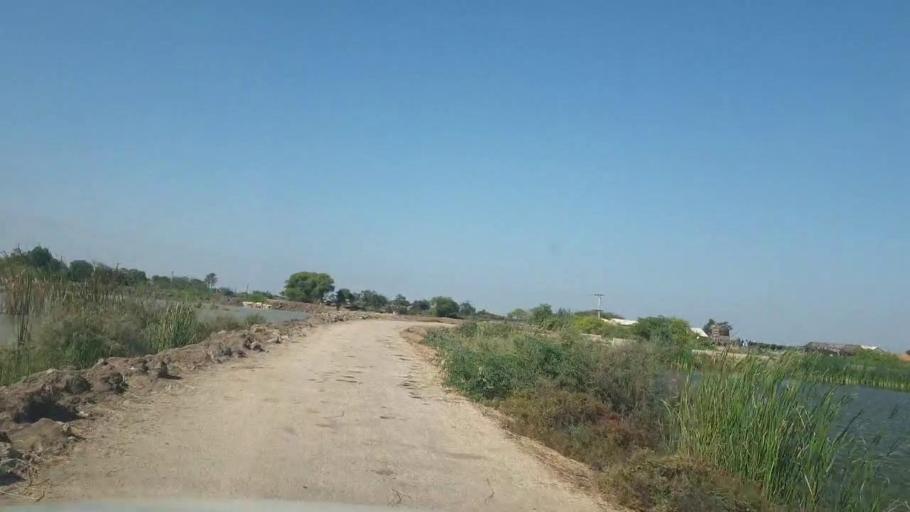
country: PK
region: Sindh
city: Chuhar Jamali
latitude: 24.4682
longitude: 67.8605
